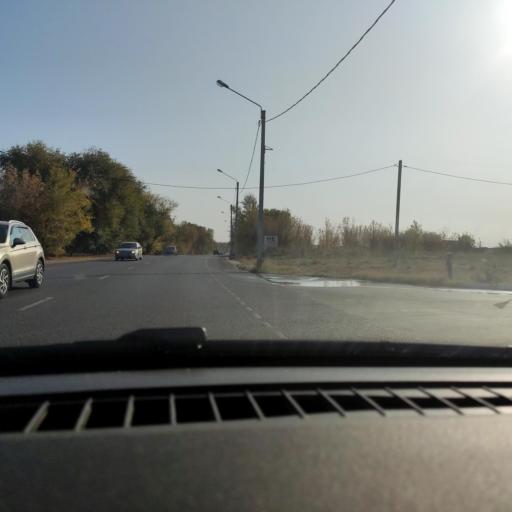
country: RU
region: Voronezj
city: Voronezh
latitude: 51.6160
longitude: 39.1786
